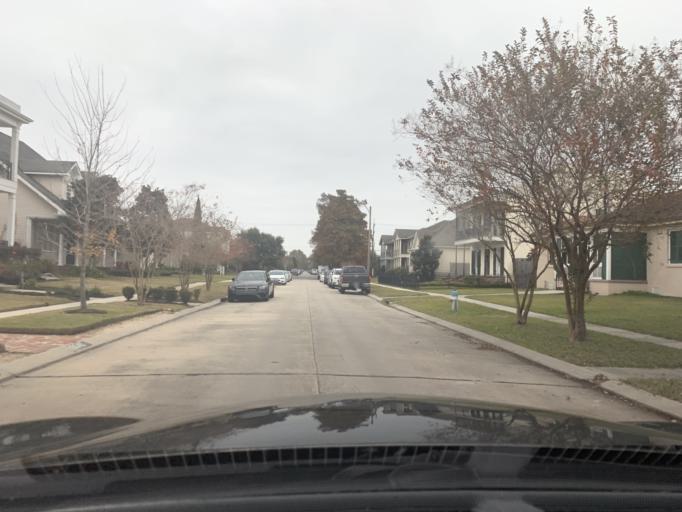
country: US
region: Louisiana
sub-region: Jefferson Parish
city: Metairie
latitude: 30.0111
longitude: -90.1060
